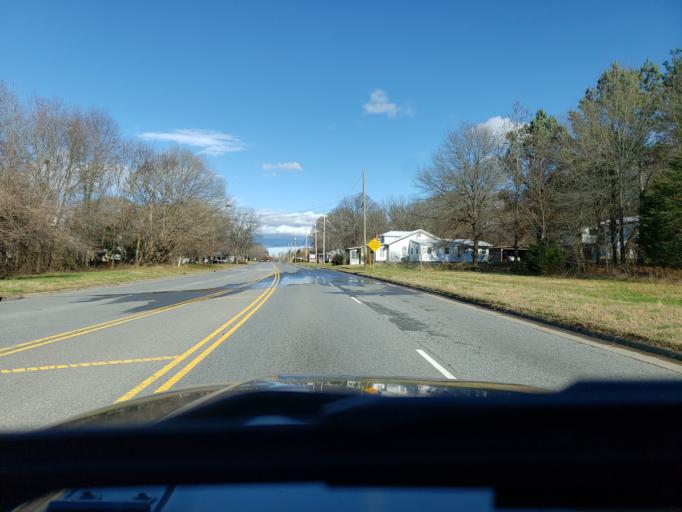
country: US
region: North Carolina
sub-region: Cleveland County
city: Shelby
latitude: 35.2669
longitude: -81.5429
